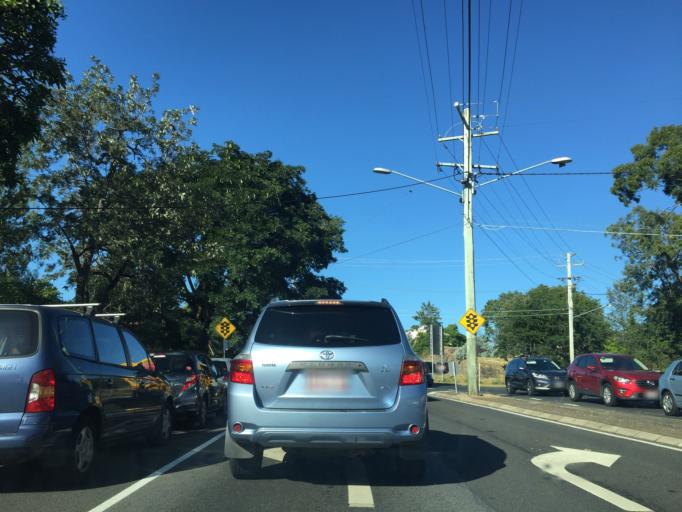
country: AU
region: Queensland
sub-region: Brisbane
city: Milton
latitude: -27.4571
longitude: 152.9858
